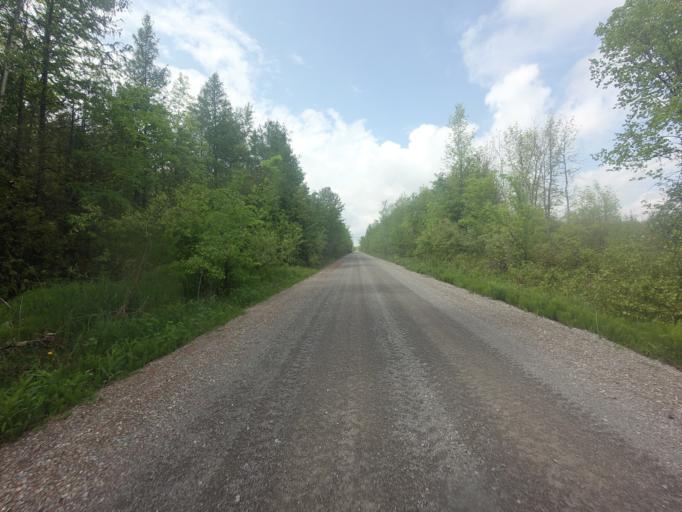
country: CA
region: Ontario
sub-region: Lanark County
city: Smiths Falls
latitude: 44.9426
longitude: -76.0403
